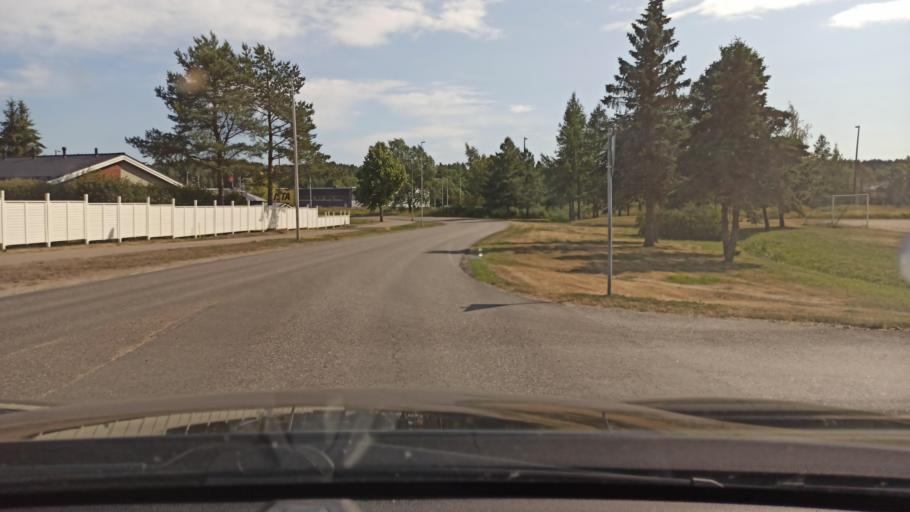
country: FI
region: Uusimaa
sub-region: Helsinki
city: Kirkkonummi
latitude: 60.1212
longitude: 24.4284
